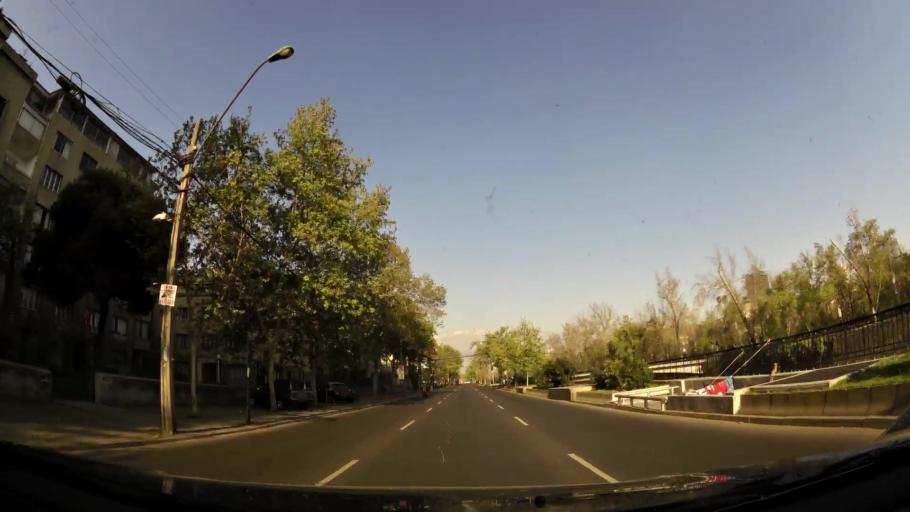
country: CL
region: Santiago Metropolitan
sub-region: Provincia de Santiago
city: Santiago
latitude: -33.4332
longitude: -70.6462
